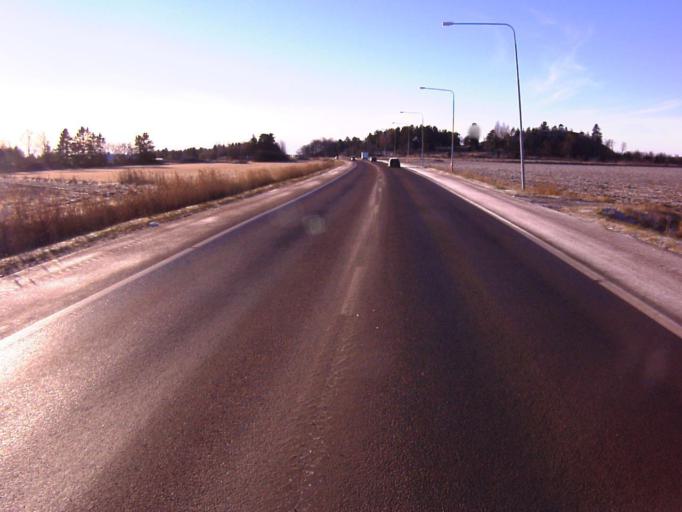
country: SE
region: Soedermanland
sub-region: Eskilstuna Kommun
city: Torshalla
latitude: 59.4045
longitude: 16.4769
